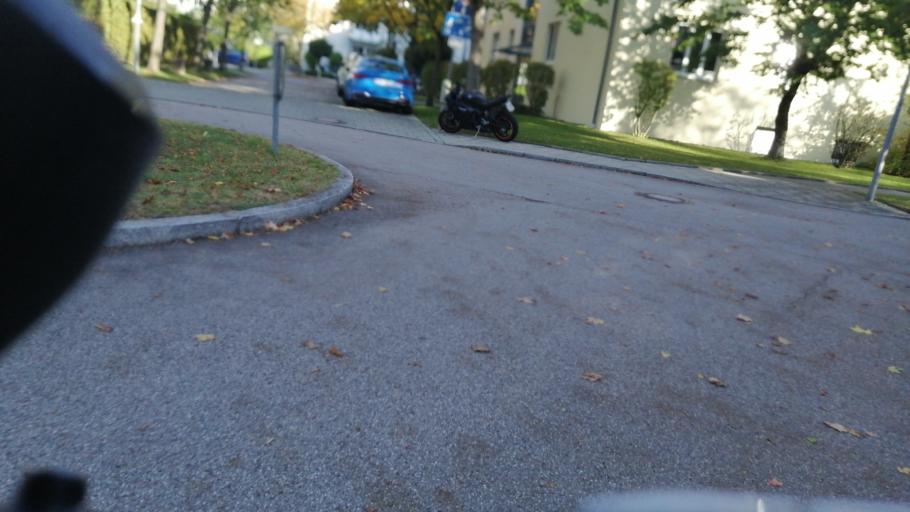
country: DE
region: Bavaria
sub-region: Upper Bavaria
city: Unterfoehring
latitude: 48.2080
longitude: 11.6019
